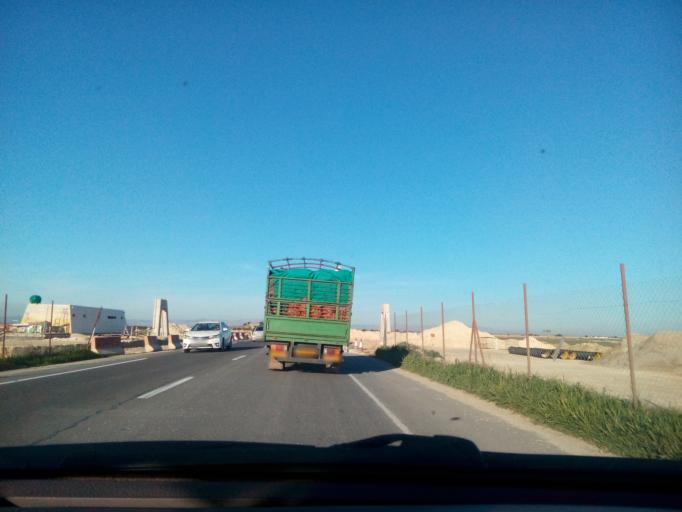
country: DZ
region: Relizane
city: Relizane
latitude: 35.7914
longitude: 0.5347
